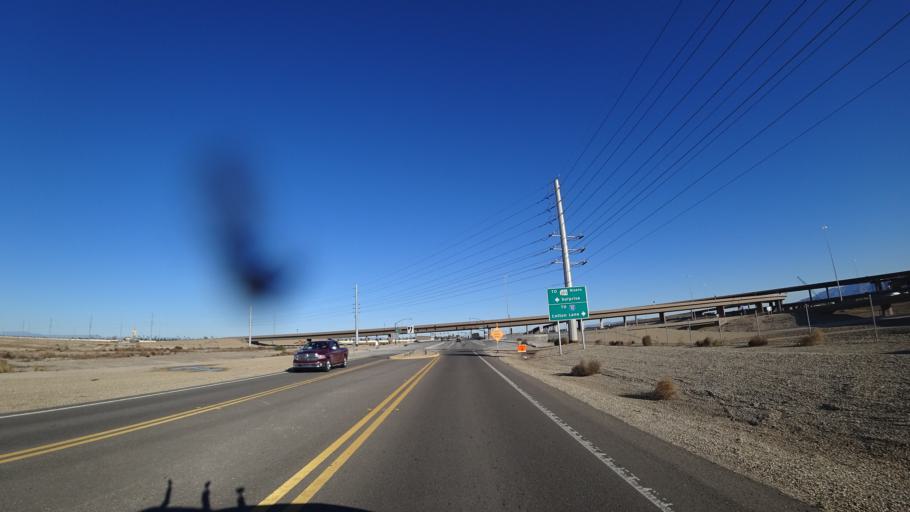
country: US
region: Arizona
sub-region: Maricopa County
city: Goodyear
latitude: 33.4646
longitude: -112.4307
